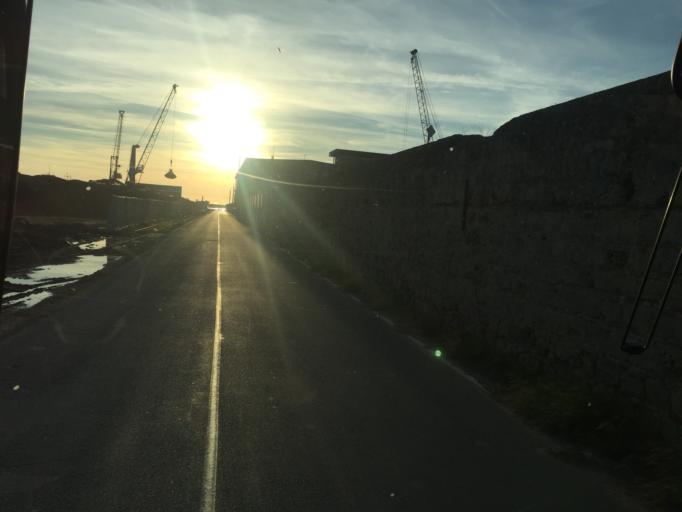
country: IT
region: Tuscany
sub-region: Provincia di Livorno
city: Livorno
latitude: 43.5543
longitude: 10.2993
